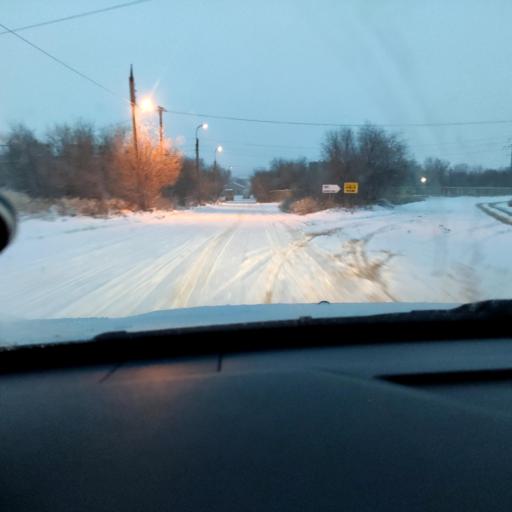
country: RU
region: Samara
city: Smyshlyayevka
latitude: 53.2395
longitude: 50.4806
